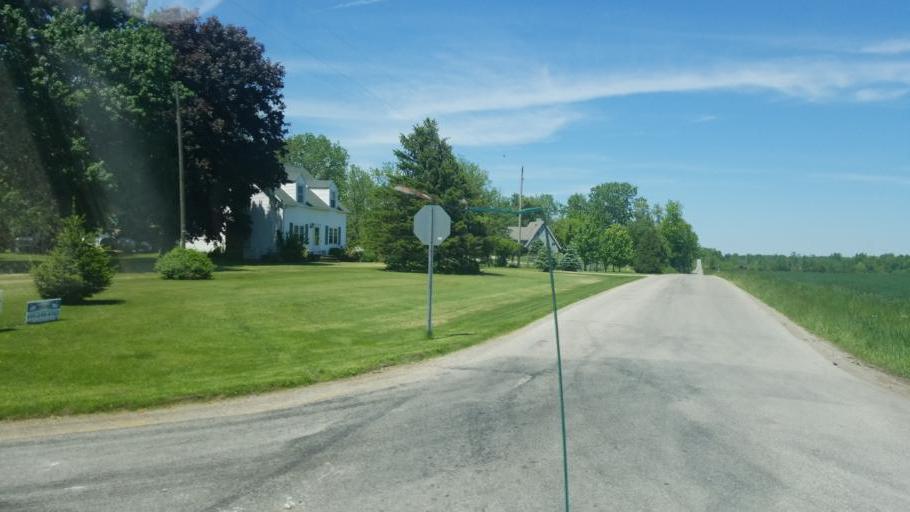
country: US
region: Ohio
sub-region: Huron County
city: Greenwich
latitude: 41.0665
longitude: -82.5366
